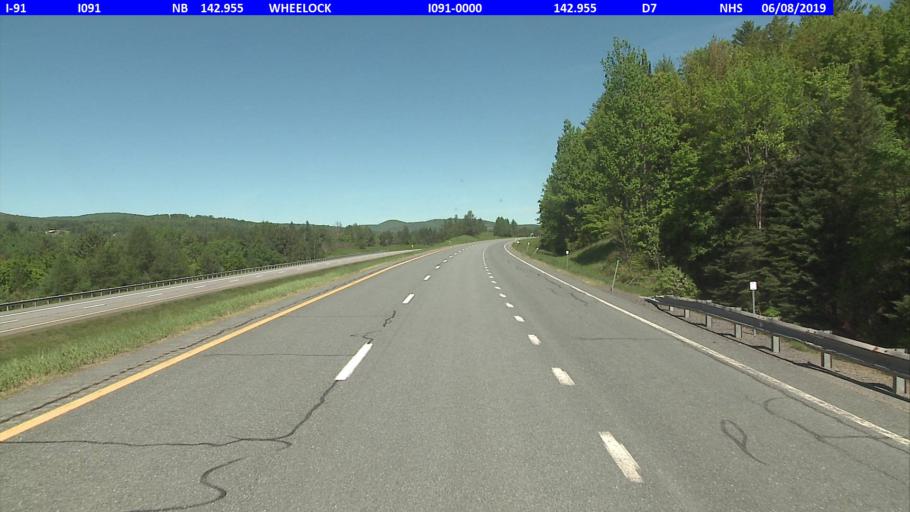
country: US
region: Vermont
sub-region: Caledonia County
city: Lyndonville
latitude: 44.5842
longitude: -72.0664
